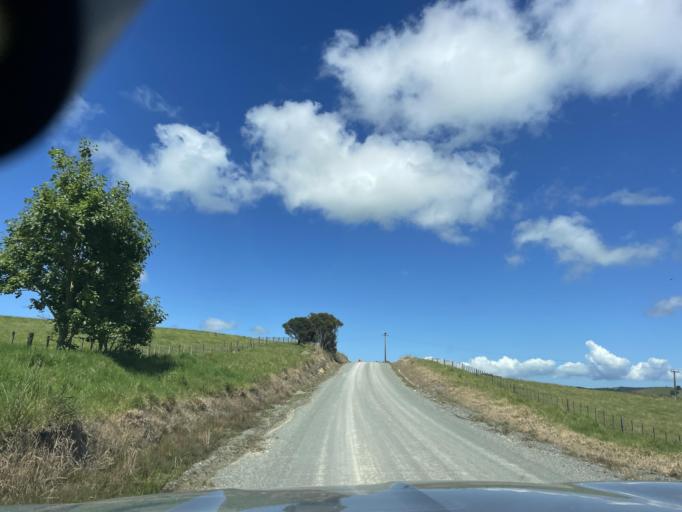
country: NZ
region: Auckland
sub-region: Auckland
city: Wellsford
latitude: -36.2761
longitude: 174.3682
